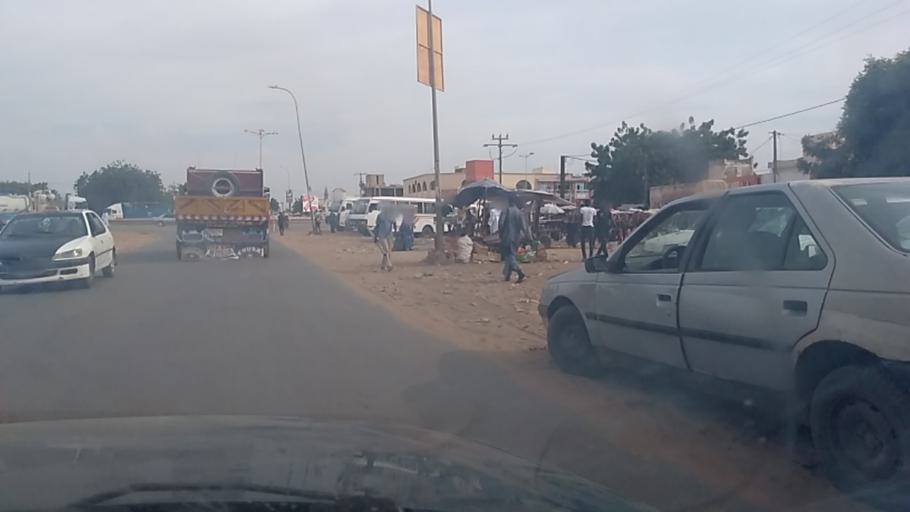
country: SN
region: Diourbel
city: Touba
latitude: 14.8426
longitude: -15.8874
